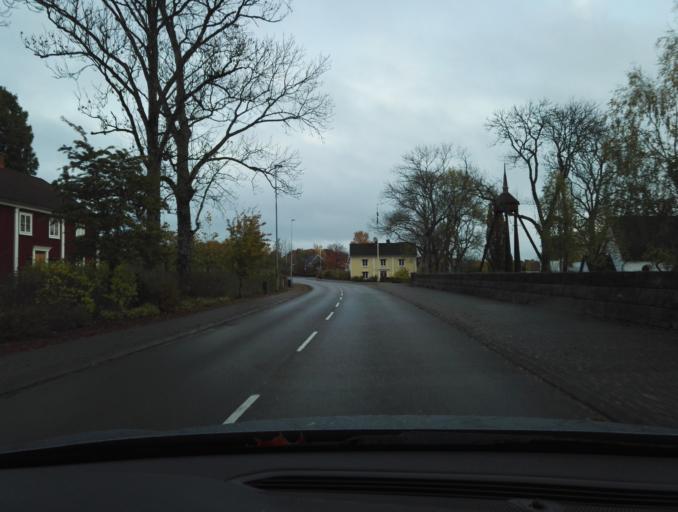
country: SE
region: Kronoberg
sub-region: Vaxjo Kommun
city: Vaexjoe
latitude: 56.9063
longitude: 14.7393
